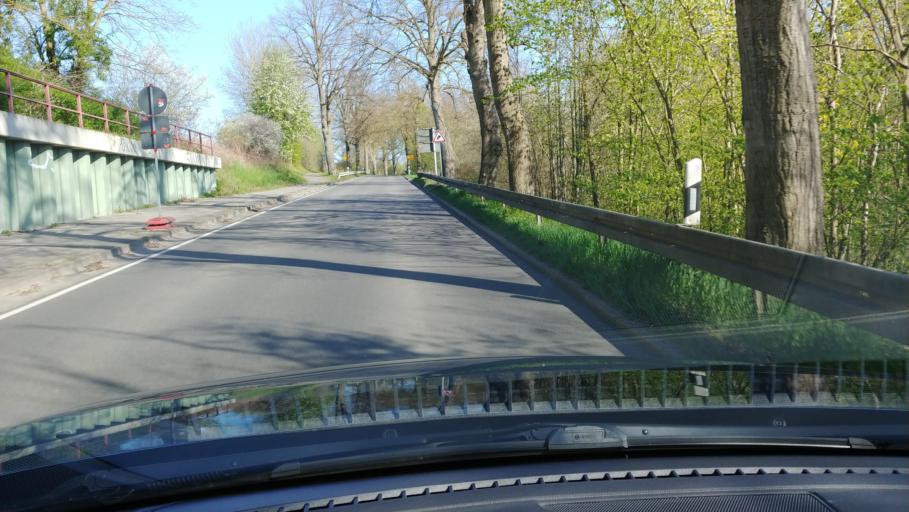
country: DE
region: Mecklenburg-Vorpommern
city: Muhlen Eichsen
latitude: 53.7589
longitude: 11.2536
